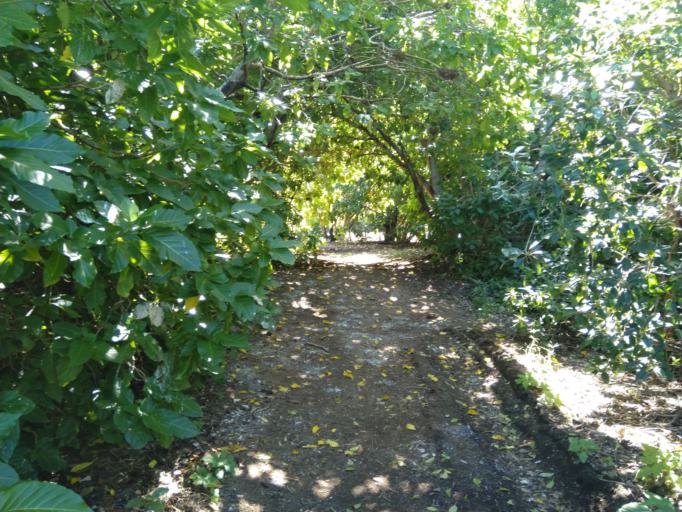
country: AU
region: Queensland
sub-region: Bundaberg
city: Bundaberg
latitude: -24.1144
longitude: 152.7143
